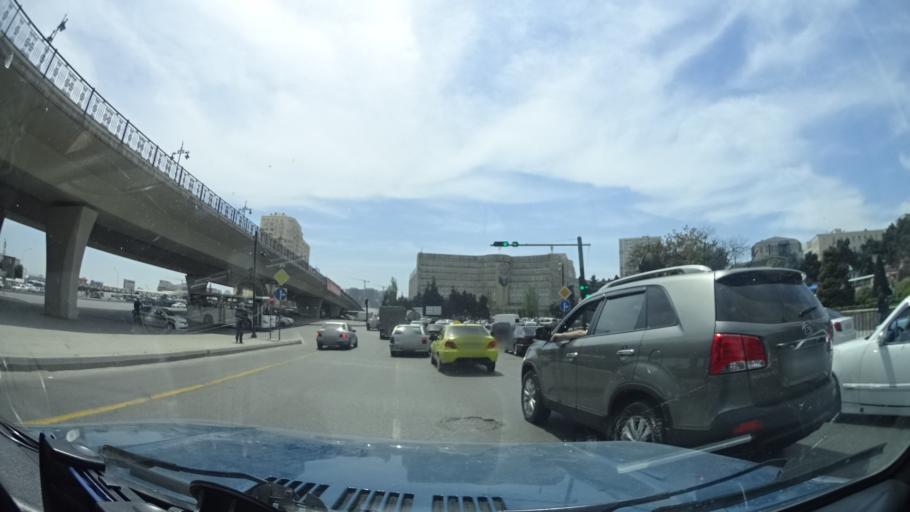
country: AZ
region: Baki
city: Khodzhi-Gasan
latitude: 40.4047
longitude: 49.8071
